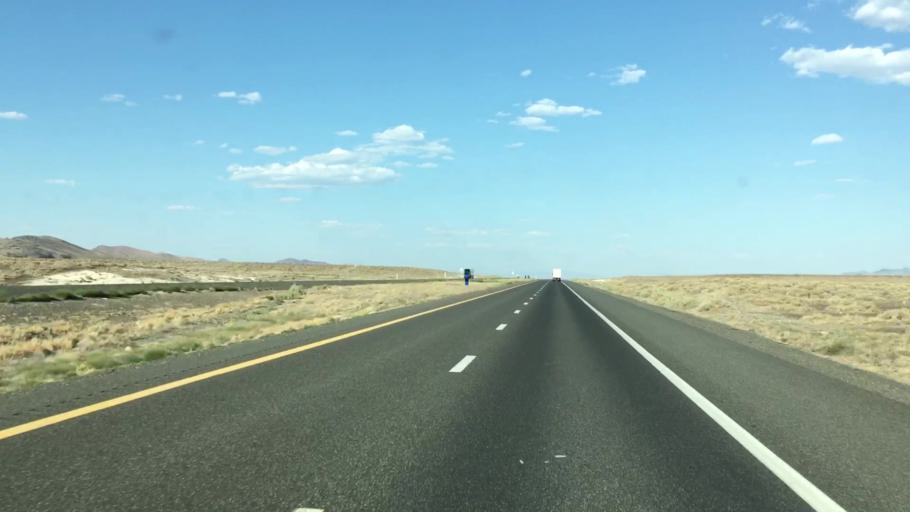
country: US
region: Nevada
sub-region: Churchill County
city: Fallon
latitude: 39.8577
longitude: -118.9167
